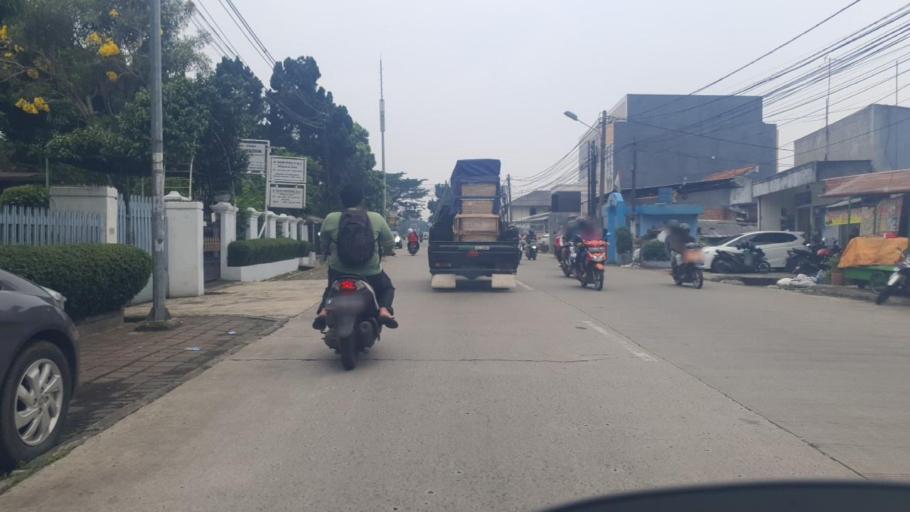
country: ID
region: West Java
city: Bogor
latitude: -6.5862
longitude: 106.7877
